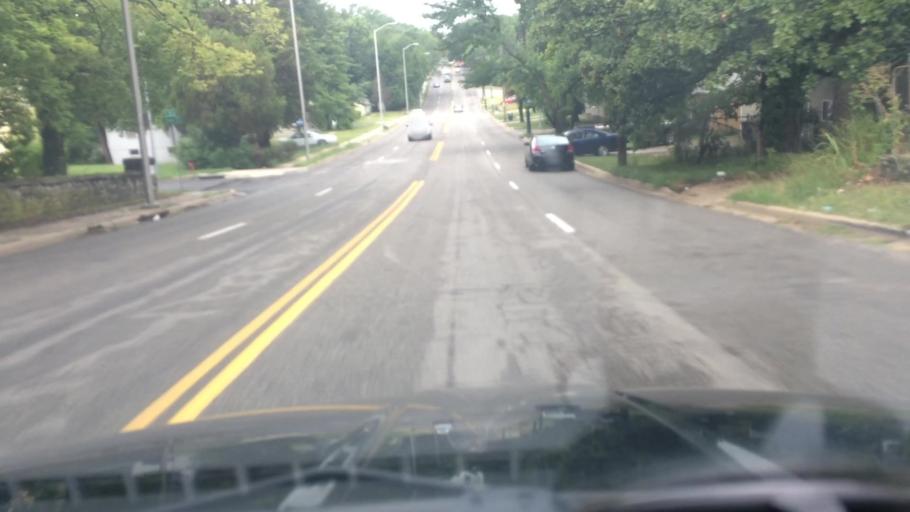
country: US
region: Kansas
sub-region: Johnson County
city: Leawood
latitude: 38.9910
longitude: -94.5609
